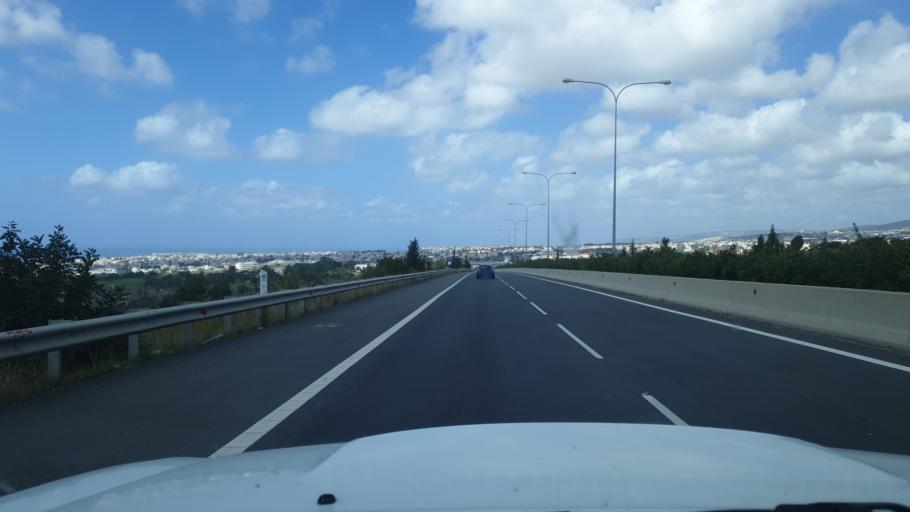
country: CY
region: Pafos
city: Paphos
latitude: 34.7742
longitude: 32.4615
